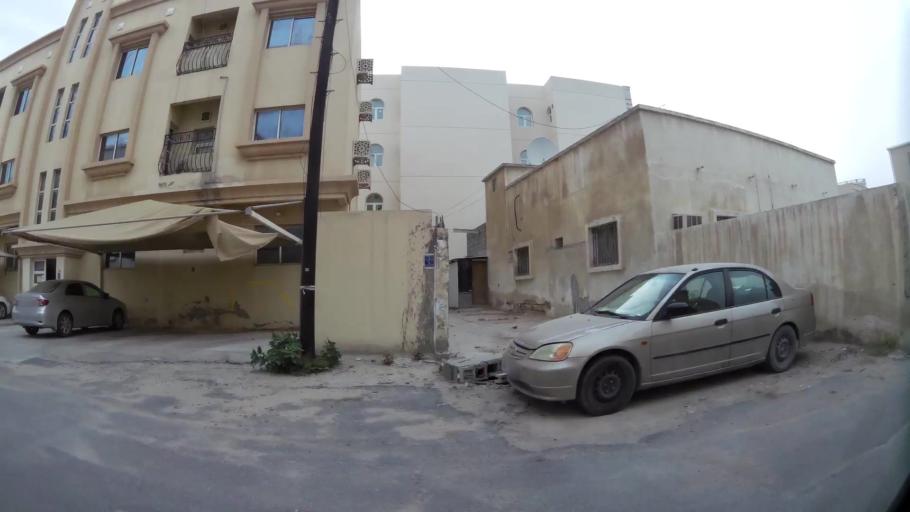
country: QA
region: Baladiyat ad Dawhah
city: Doha
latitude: 25.3041
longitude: 51.4945
